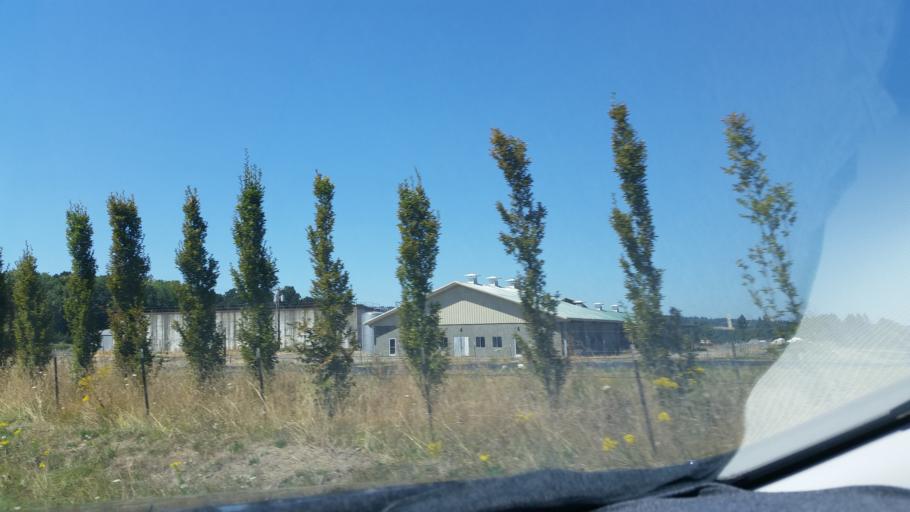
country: US
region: Oregon
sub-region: Clackamas County
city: Wilsonville
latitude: 45.2596
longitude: -122.8280
